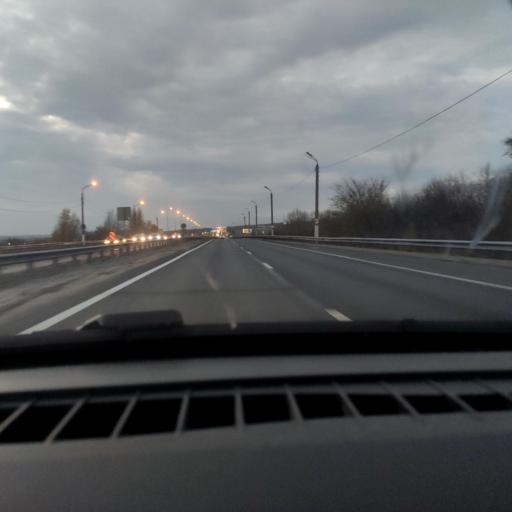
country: RU
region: Voronezj
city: Pridonskoy
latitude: 51.6505
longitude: 39.0728
